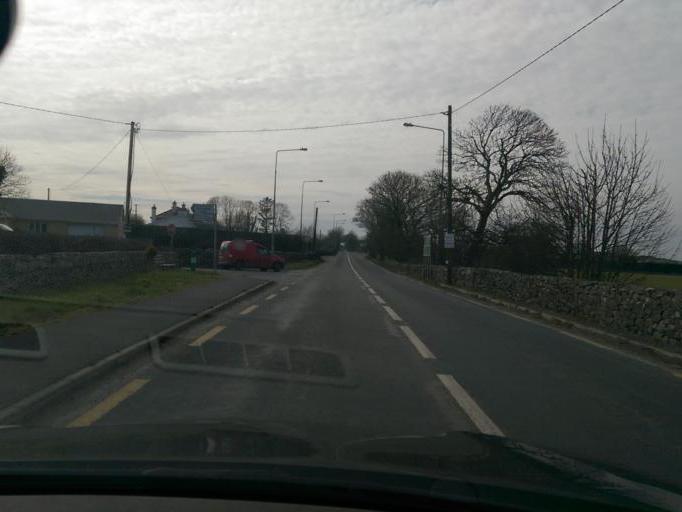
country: IE
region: Connaught
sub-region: County Galway
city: Claregalway
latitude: 53.3805
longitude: -8.8578
